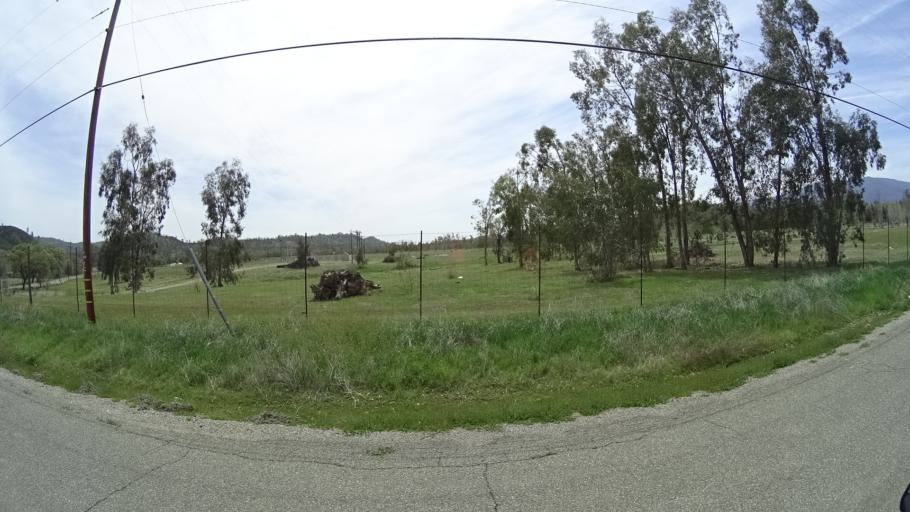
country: US
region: California
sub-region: Glenn County
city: Willows
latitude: 39.5946
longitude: -122.5437
